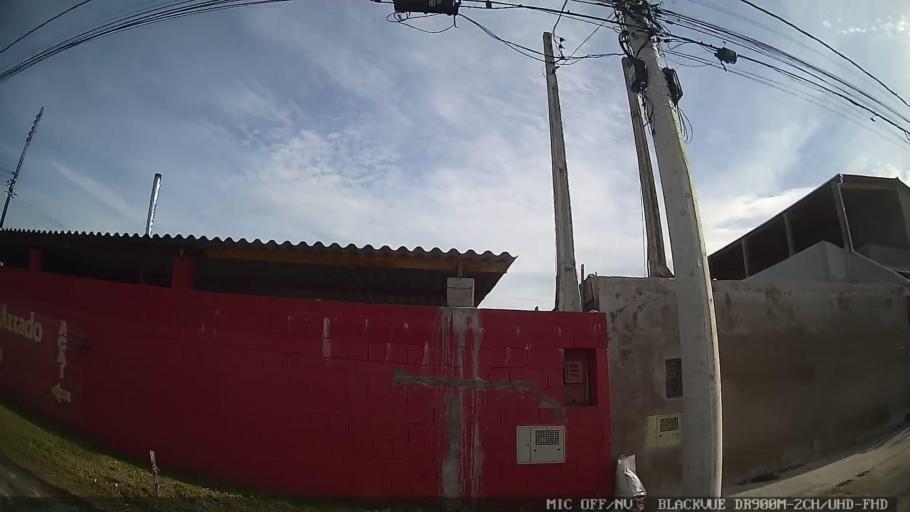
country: BR
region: Sao Paulo
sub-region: Itanhaem
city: Itanhaem
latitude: -24.1622
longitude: -46.7672
